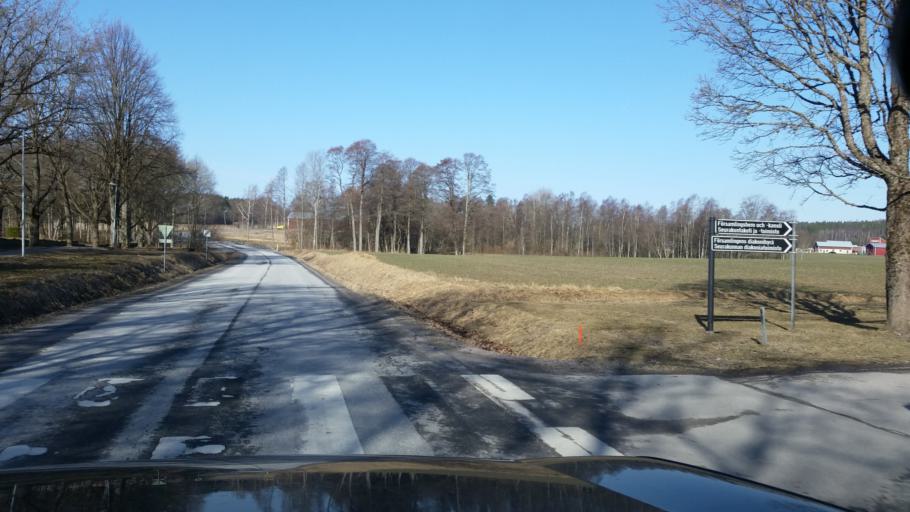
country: FI
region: Uusimaa
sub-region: Raaseporin
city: Inga
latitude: 60.0459
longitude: 24.0027
